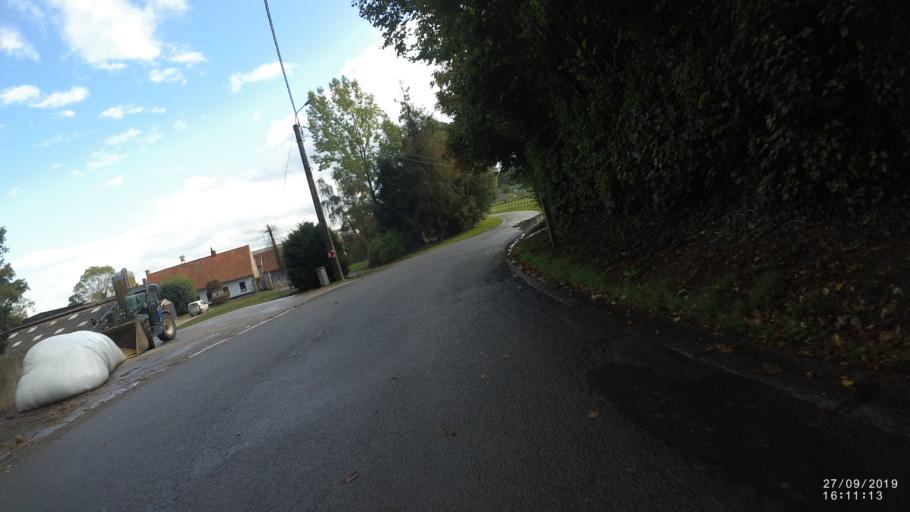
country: BE
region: Flanders
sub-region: Provincie Oost-Vlaanderen
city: Zottegem
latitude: 50.8645
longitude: 3.7543
